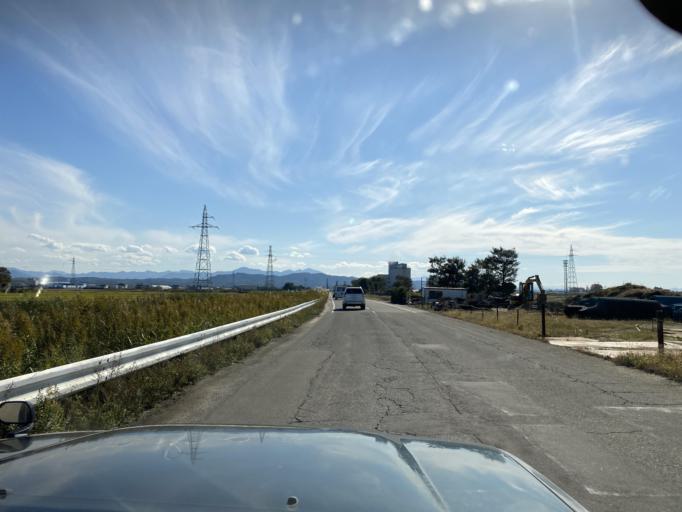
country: JP
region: Niigata
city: Niitsu-honcho
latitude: 37.7989
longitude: 139.0769
